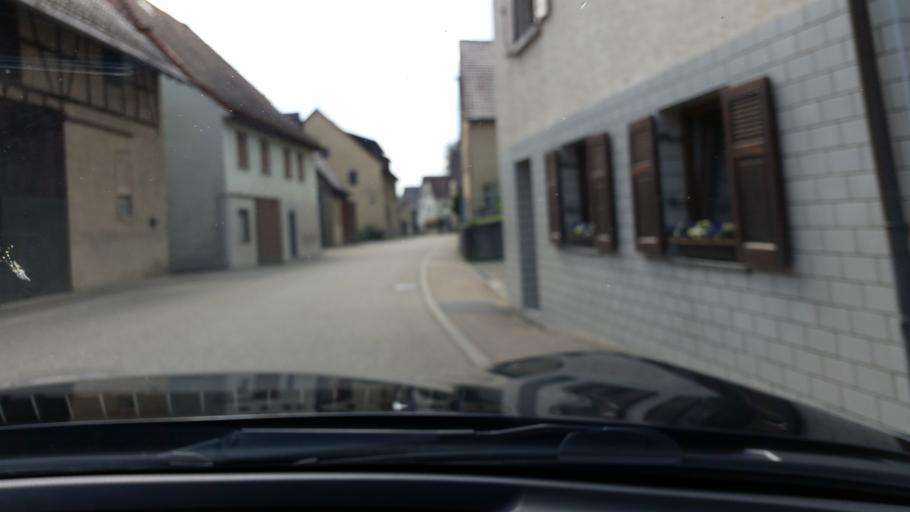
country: DE
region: Baden-Wuerttemberg
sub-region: Regierungsbezirk Stuttgart
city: Forchtenberg
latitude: 49.3462
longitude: 9.5308
